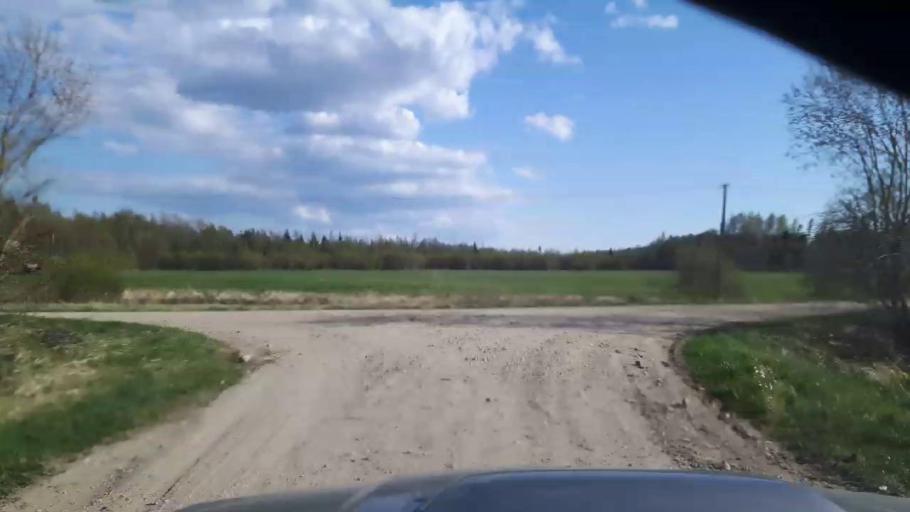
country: EE
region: Paernumaa
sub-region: Tootsi vald
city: Tootsi
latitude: 58.4135
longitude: 24.8522
